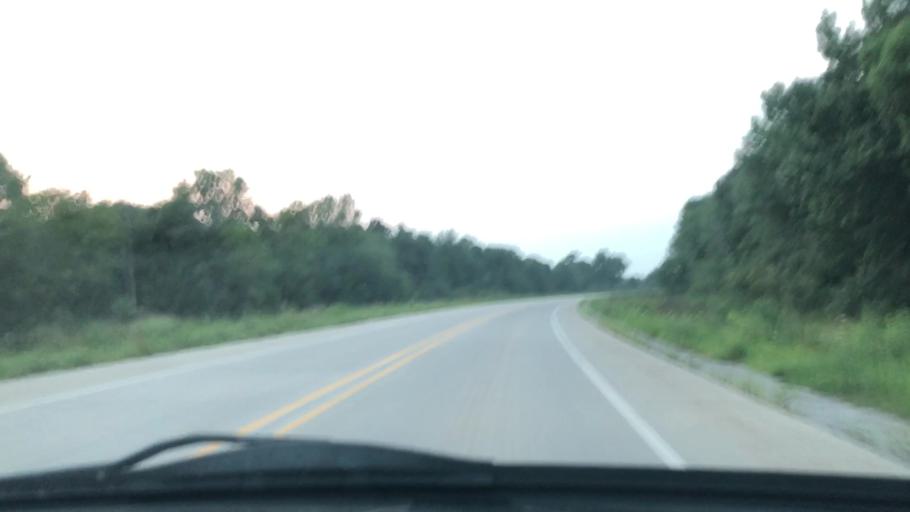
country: US
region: Iowa
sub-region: Johnson County
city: North Liberty
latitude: 41.8154
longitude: -91.6680
